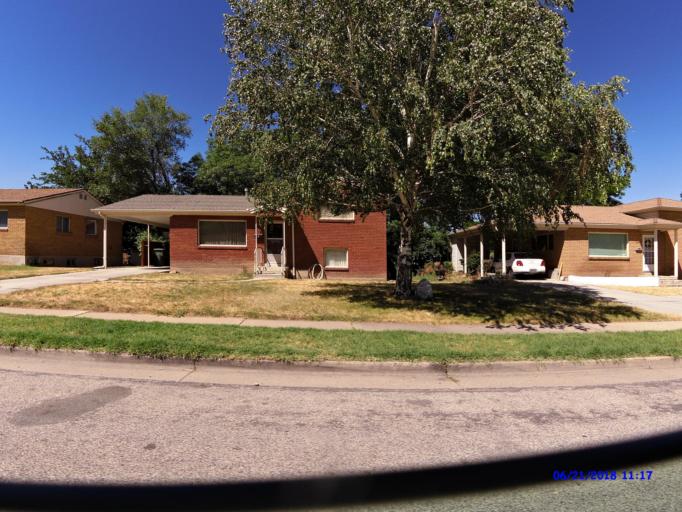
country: US
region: Utah
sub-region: Weber County
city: Ogden
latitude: 41.2539
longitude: -111.9553
